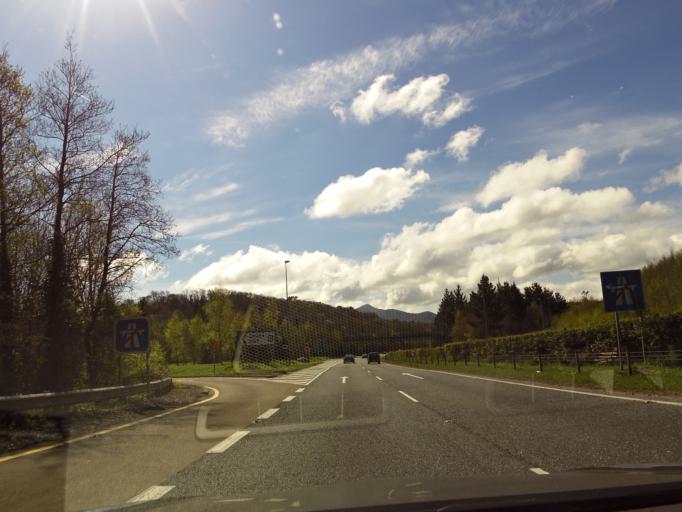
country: IE
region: Leinster
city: Little Bray
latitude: 53.1984
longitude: -6.1324
